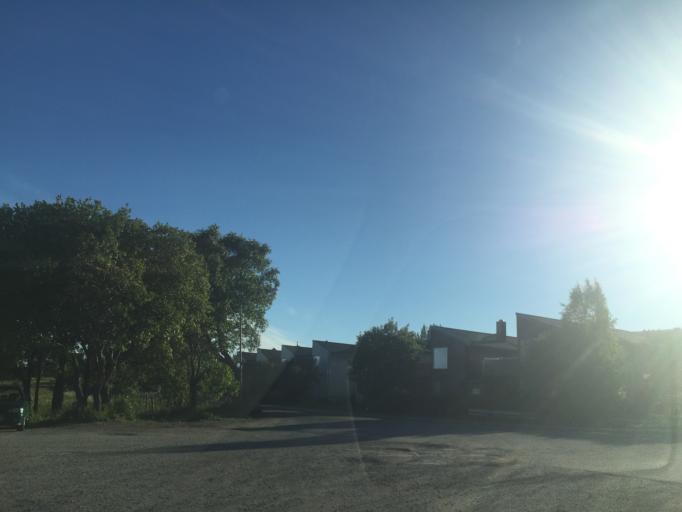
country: NO
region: Nordland
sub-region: Bodo
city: Lopsmarka
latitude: 67.2913
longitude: 14.4548
